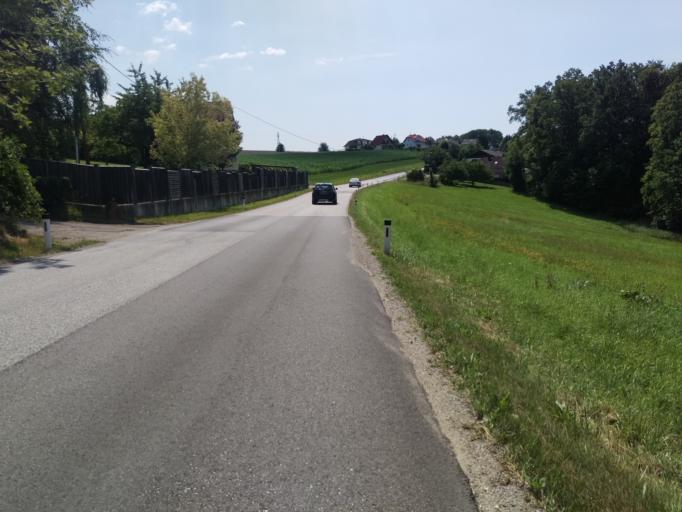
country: AT
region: Styria
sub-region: Politischer Bezirk Graz-Umgebung
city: Kumberg
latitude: 47.1452
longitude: 15.5223
